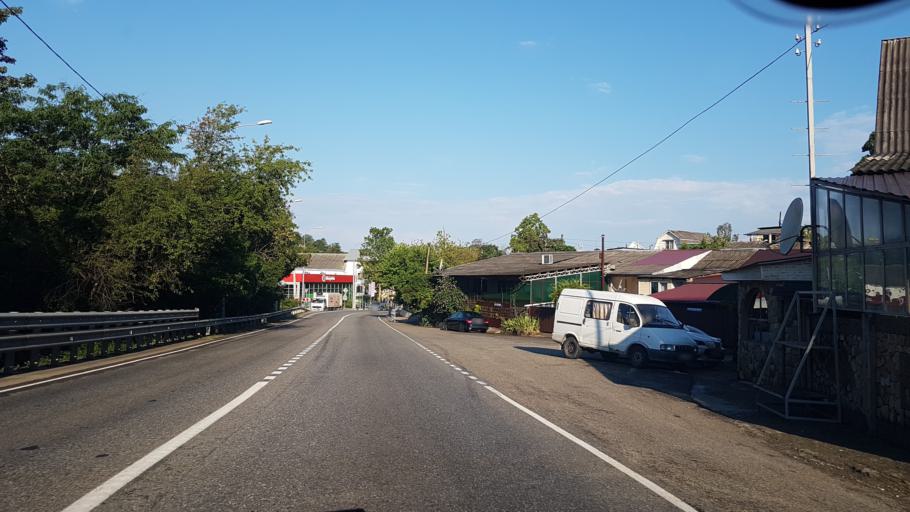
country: RU
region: Krasnodarskiy
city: Vardane
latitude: 43.7288
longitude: 39.5632
